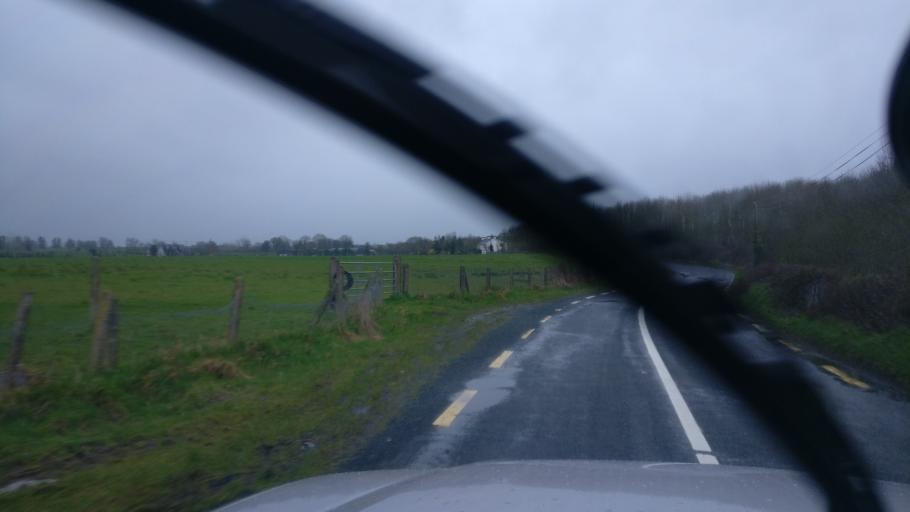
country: IE
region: Connaught
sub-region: County Galway
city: Loughrea
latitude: 53.0990
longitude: -8.4131
